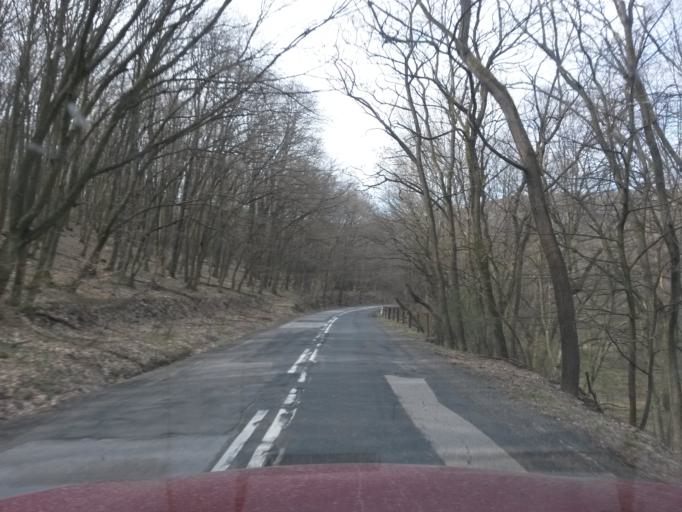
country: SK
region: Nitriansky
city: Sahy
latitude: 48.1668
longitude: 19.0199
